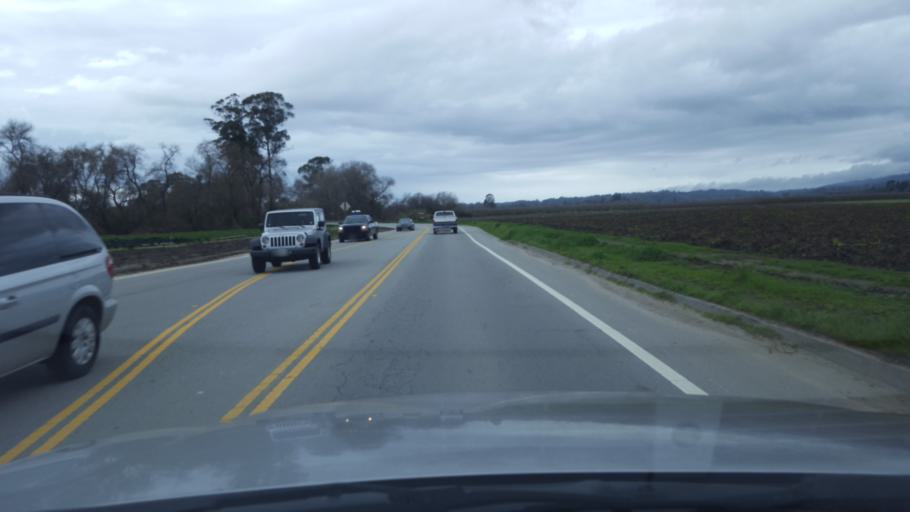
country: US
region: California
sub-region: Santa Cruz County
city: Freedom
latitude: 36.9413
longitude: -121.7705
